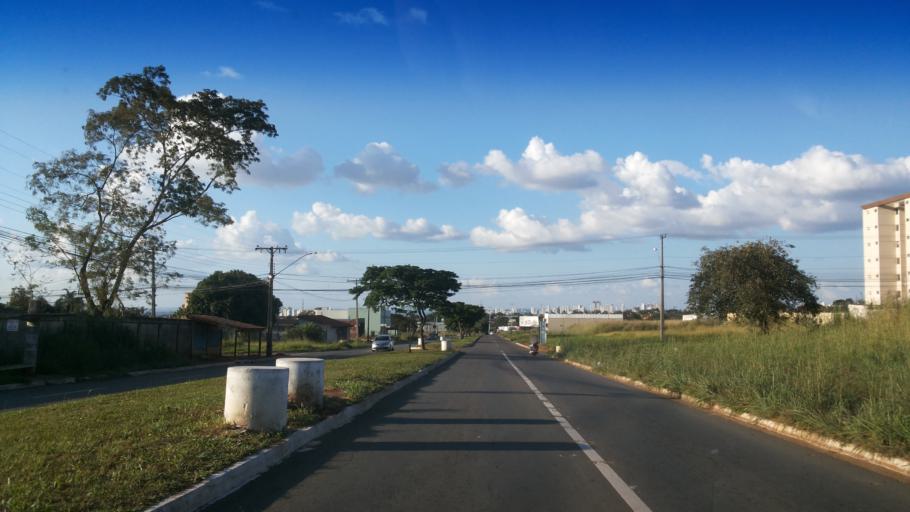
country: BR
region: Goias
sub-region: Goiania
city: Goiania
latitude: -16.7451
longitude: -49.3172
